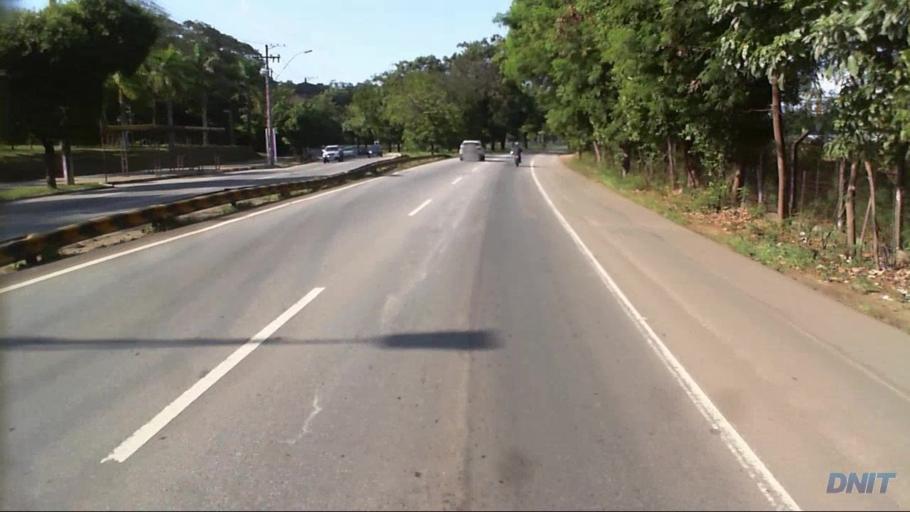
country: BR
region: Minas Gerais
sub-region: Ipatinga
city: Ipatinga
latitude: -19.4887
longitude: -42.5602
